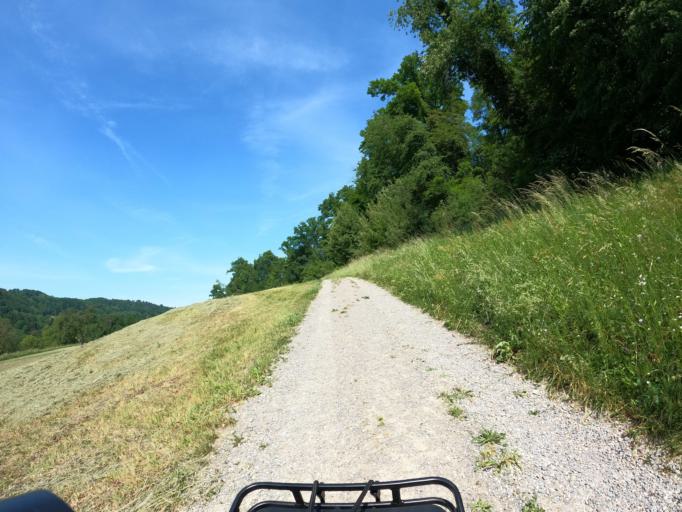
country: CH
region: Zurich
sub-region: Bezirk Buelach
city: Rorbas
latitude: 47.5408
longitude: 8.5715
